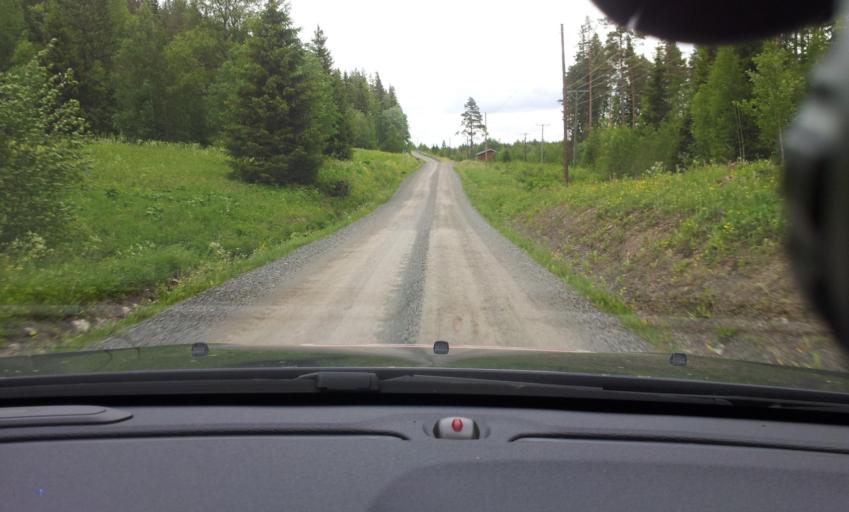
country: SE
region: Jaemtland
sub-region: OEstersunds Kommun
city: Brunflo
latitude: 62.9685
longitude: 14.6941
